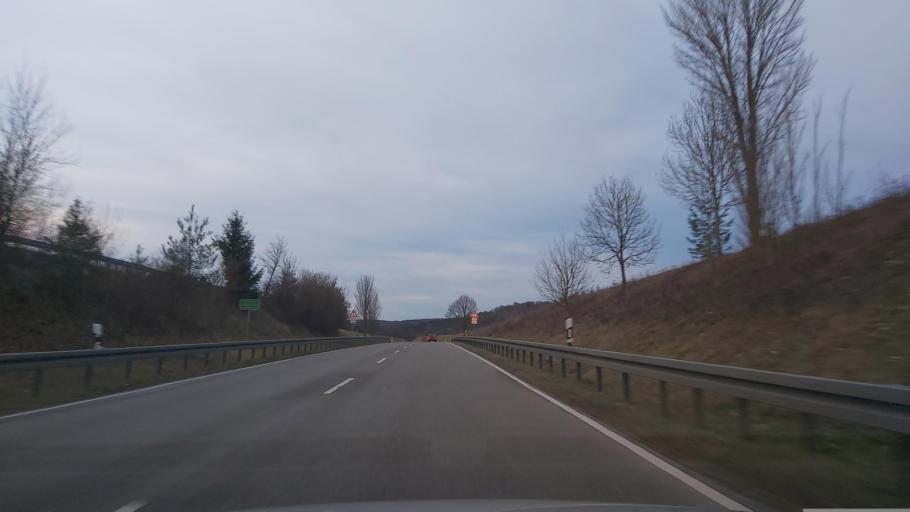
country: DE
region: Baden-Wuerttemberg
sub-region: Tuebingen Region
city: Munsingen
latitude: 48.4218
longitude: 9.4731
